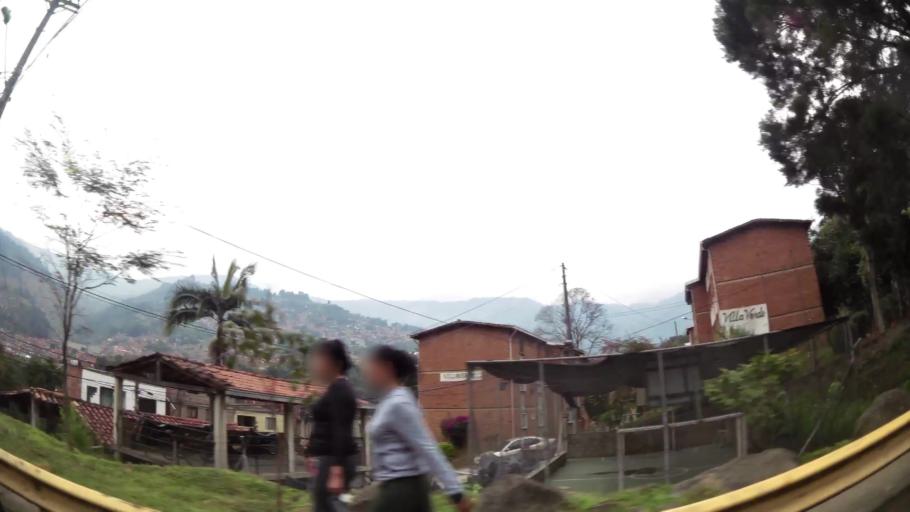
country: CO
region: Antioquia
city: Medellin
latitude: 6.2306
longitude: -75.5352
